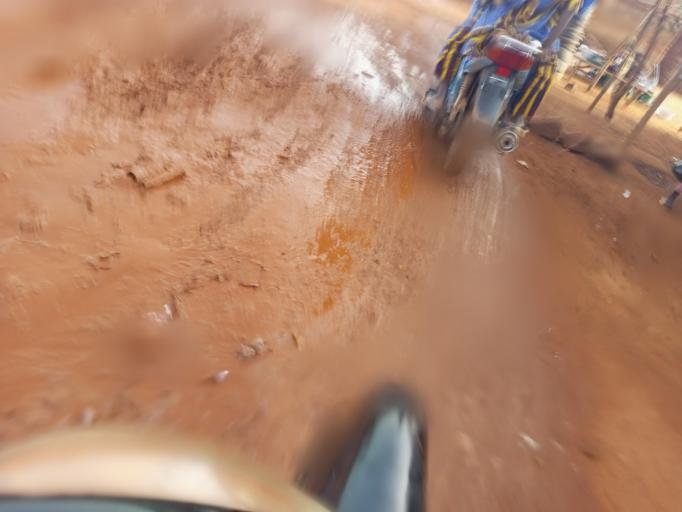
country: ML
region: Bamako
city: Bamako
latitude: 12.5235
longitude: -7.9947
